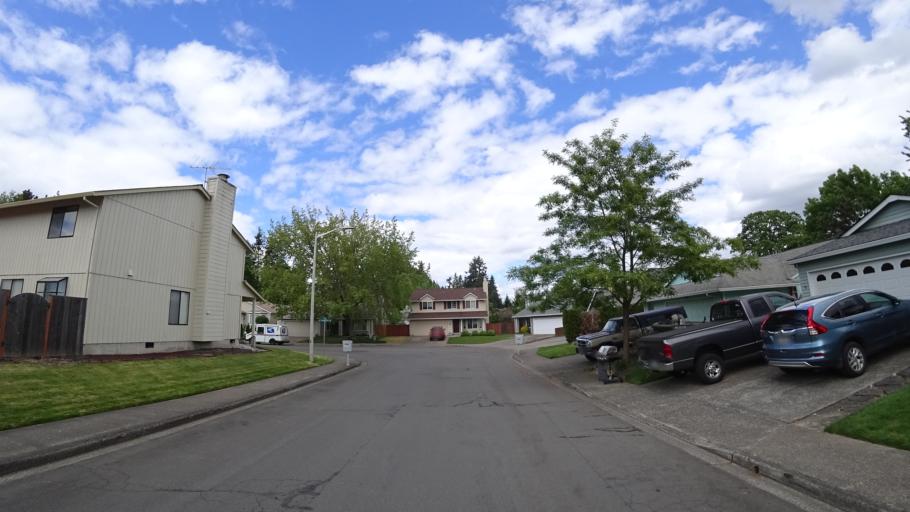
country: US
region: Oregon
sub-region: Washington County
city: Aloha
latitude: 45.4690
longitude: -122.8567
